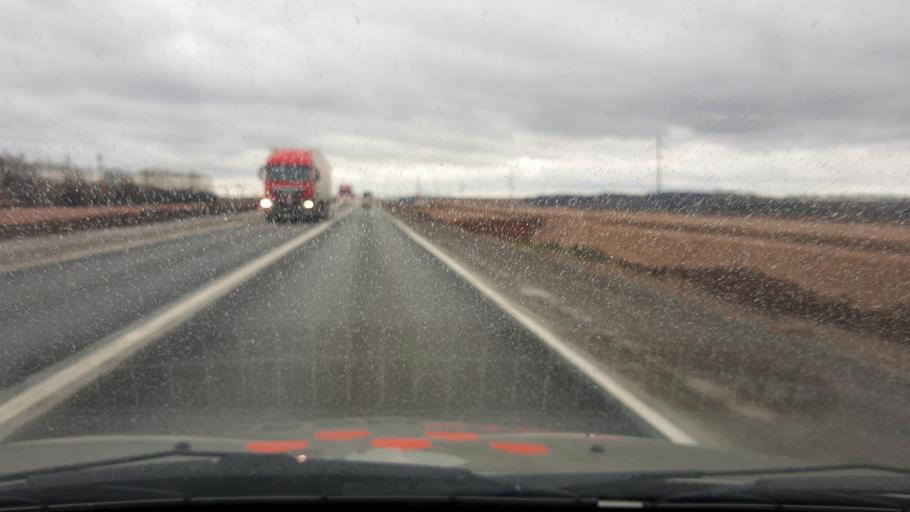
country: RU
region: Bashkortostan
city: Kabakovo
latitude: 54.7047
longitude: 56.2197
